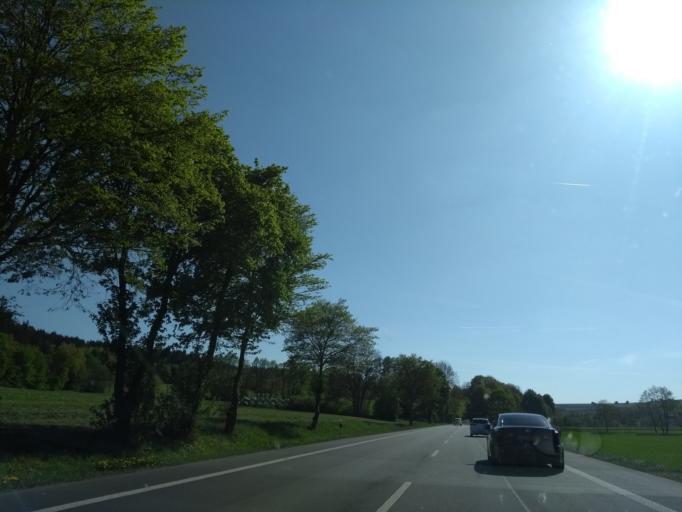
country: DE
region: Hesse
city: Frankenberg
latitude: 51.1055
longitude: 8.8449
